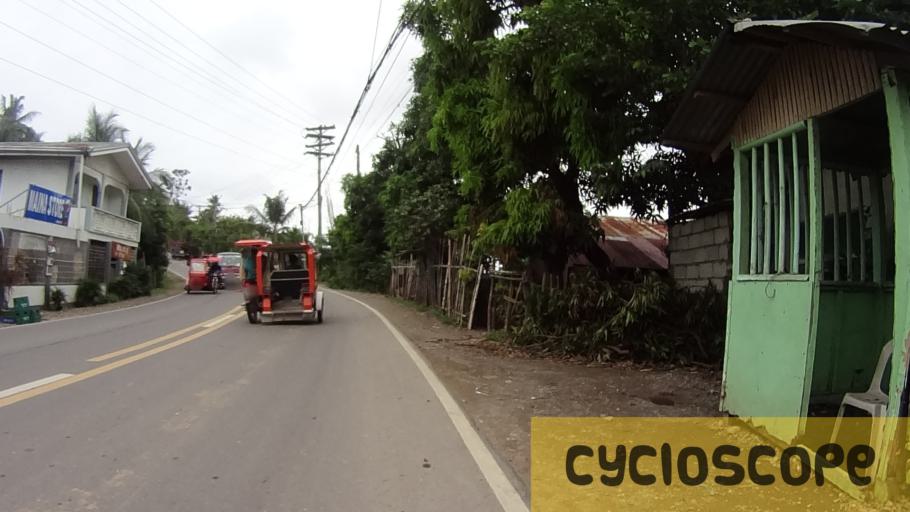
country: PH
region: Western Visayas
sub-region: Province of Aklan
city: Caticlan
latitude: 11.9324
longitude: 121.9600
